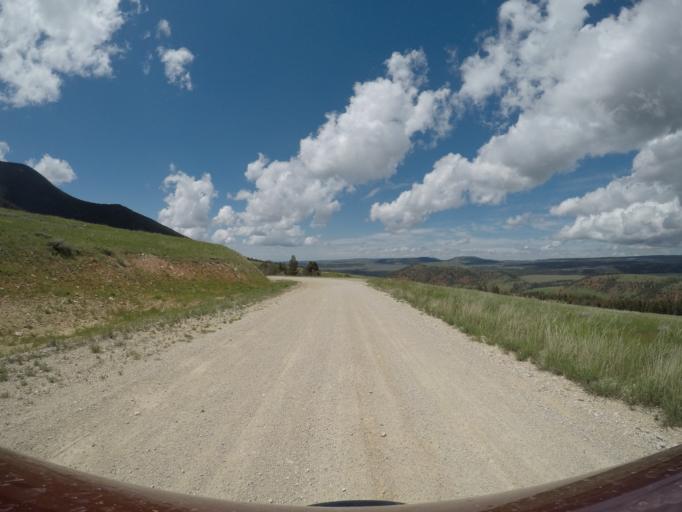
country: US
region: Wyoming
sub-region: Big Horn County
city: Lovell
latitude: 45.1891
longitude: -108.4732
